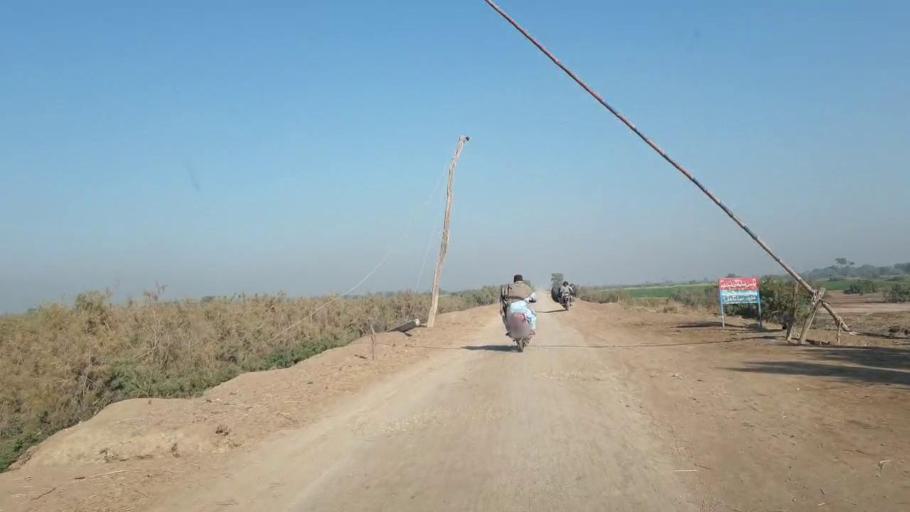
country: PK
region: Sindh
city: Shahdadpur
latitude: 25.9689
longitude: 68.4986
